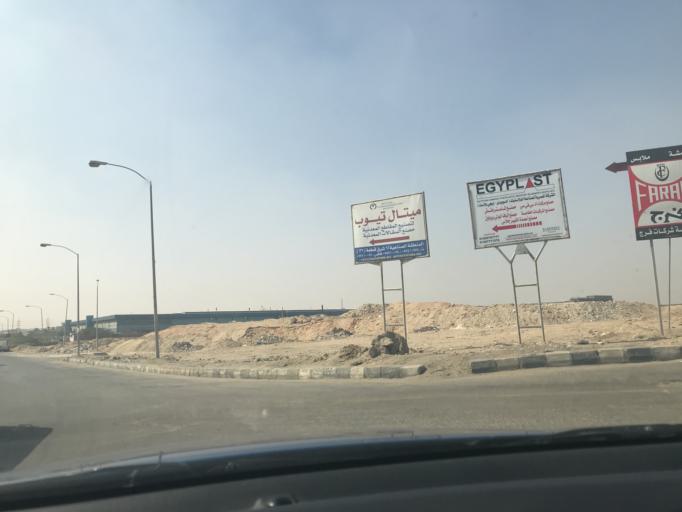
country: EG
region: Eastern Province
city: Bilbays
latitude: 30.2524
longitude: 31.7574
